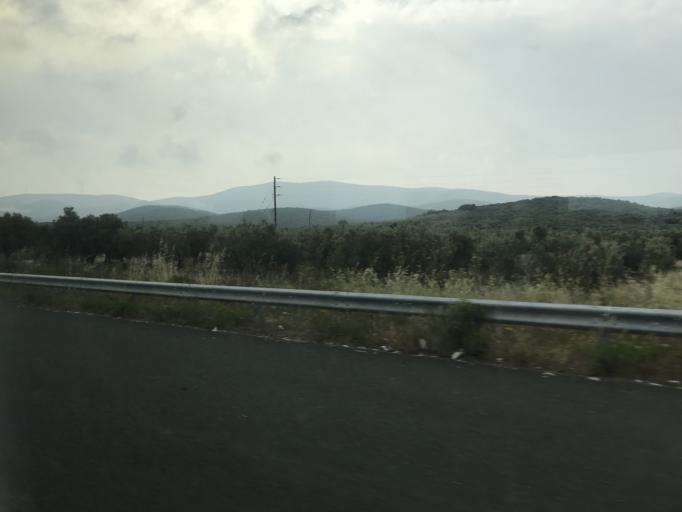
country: GR
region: East Macedonia and Thrace
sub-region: Nomos Evrou
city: Alexandroupoli
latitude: 40.8706
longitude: 25.7876
